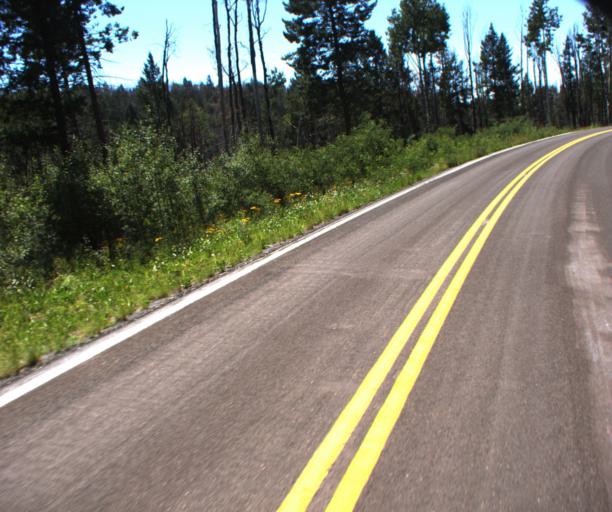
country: US
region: Arizona
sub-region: Greenlee County
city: Morenci
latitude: 33.5726
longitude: -109.3580
